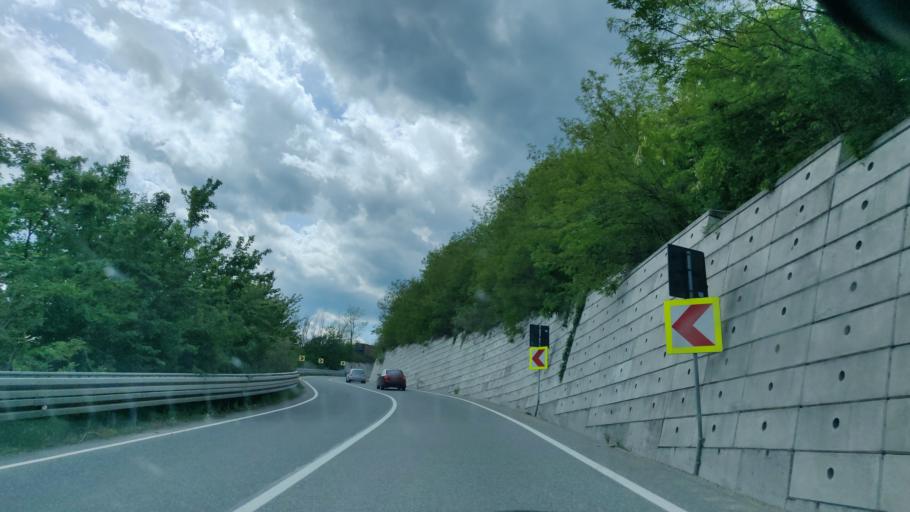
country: RO
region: Vrancea
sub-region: Comuna Negrilesti
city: Negrilesti
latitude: 45.9224
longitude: 26.6951
